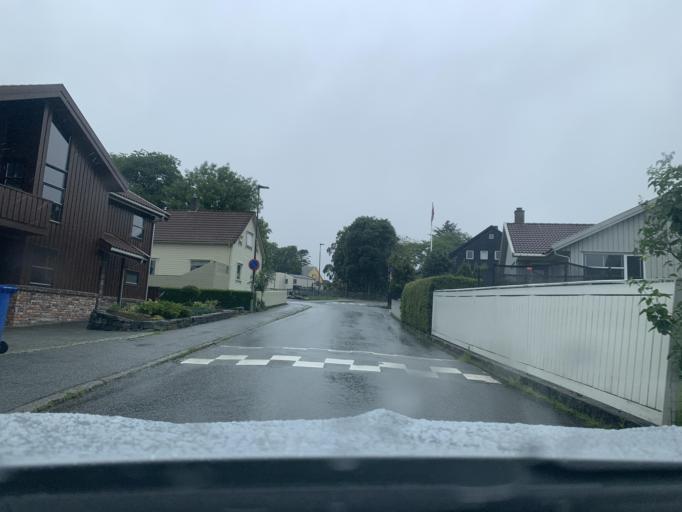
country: NO
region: Rogaland
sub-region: Time
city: Bryne
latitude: 58.7317
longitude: 5.6463
